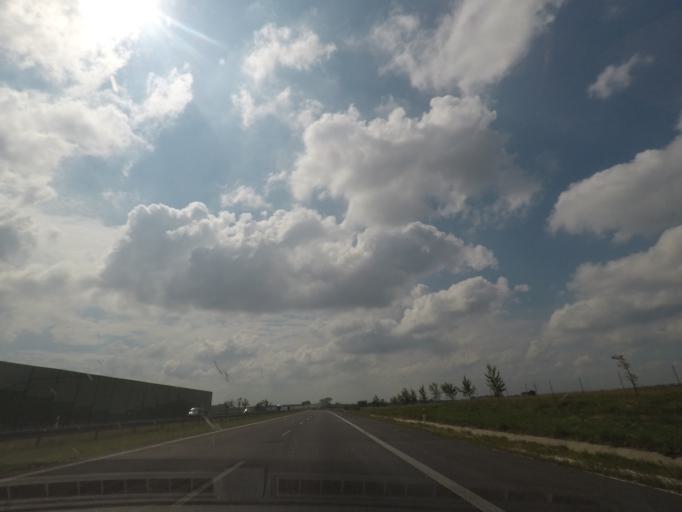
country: PL
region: Lodz Voivodeship
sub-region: Powiat kutnowski
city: Krzyzanow
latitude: 52.1537
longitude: 19.4819
